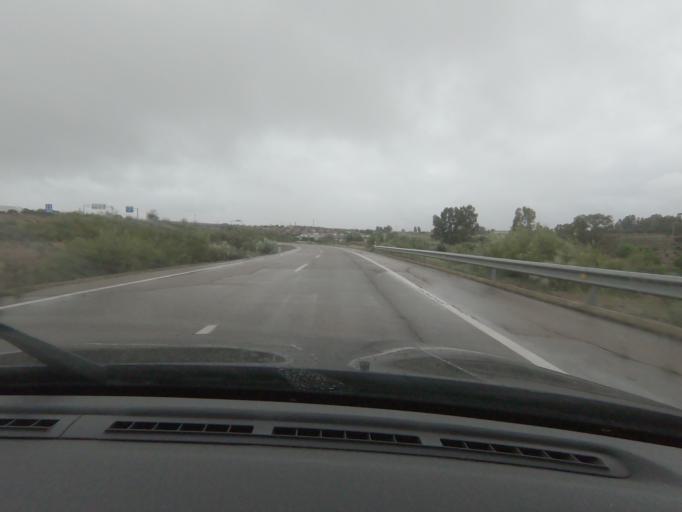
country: ES
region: Extremadura
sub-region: Provincia de Badajoz
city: Calamonte
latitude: 38.9060
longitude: -6.3762
